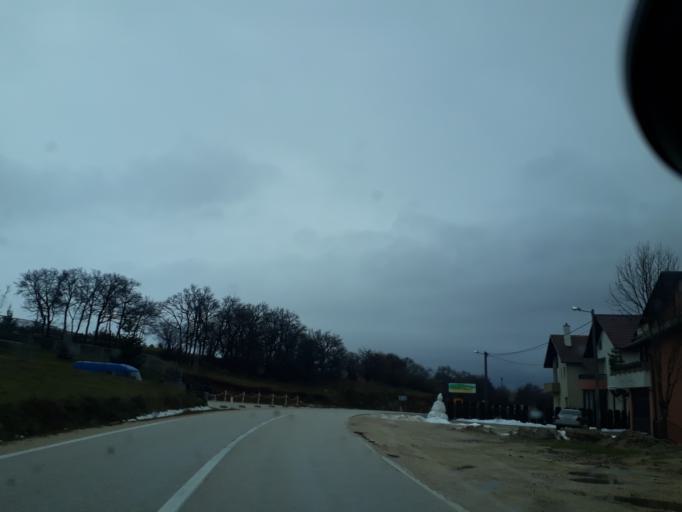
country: BA
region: Federation of Bosnia and Herzegovina
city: Tomislavgrad
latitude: 43.8364
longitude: 17.1869
